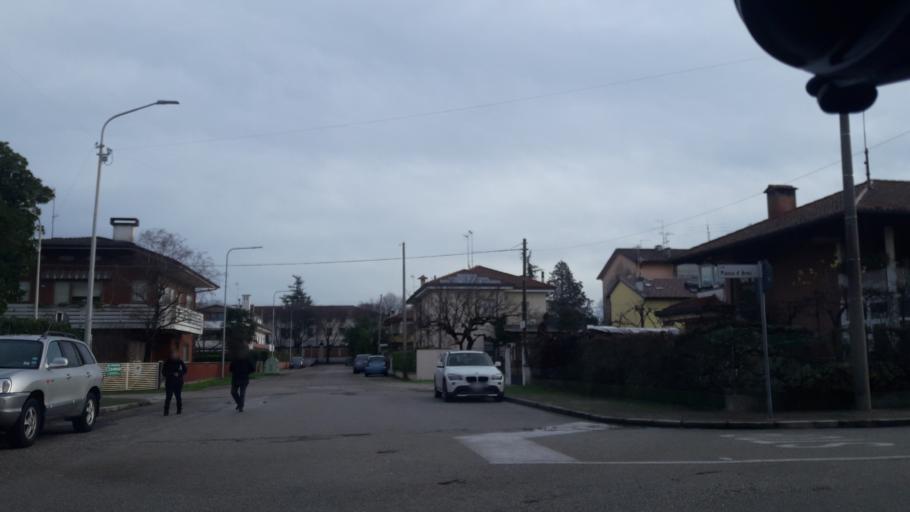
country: IT
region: Friuli Venezia Giulia
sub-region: Provincia di Udine
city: Udine
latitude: 46.0685
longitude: 13.2517
